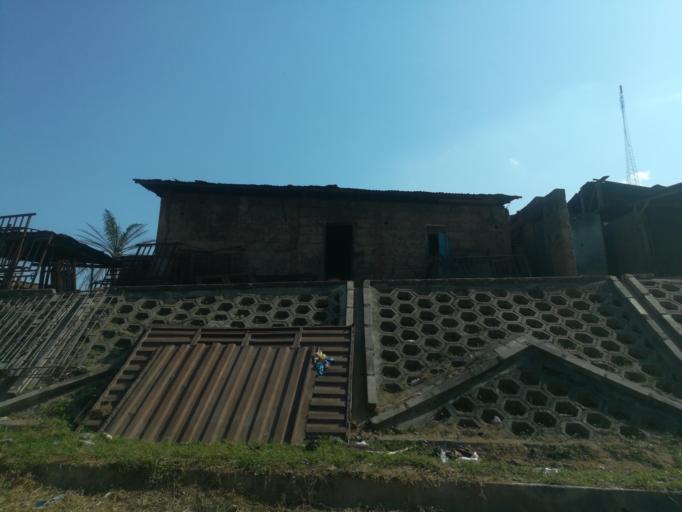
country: NG
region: Ogun
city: Abeokuta
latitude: 7.1566
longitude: 3.3364
